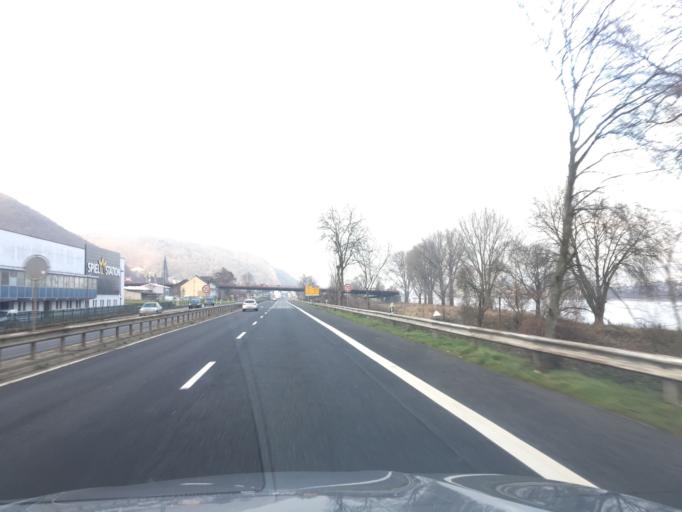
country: DE
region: Rheinland-Pfalz
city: Brohl-Lutzing
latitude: 50.4813
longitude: 7.3348
